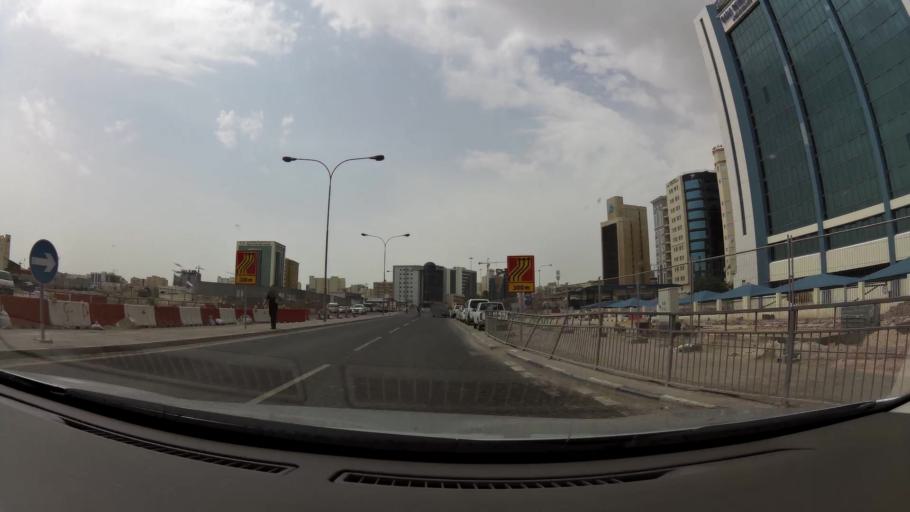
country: QA
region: Baladiyat ad Dawhah
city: Doha
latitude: 25.2797
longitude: 51.5312
